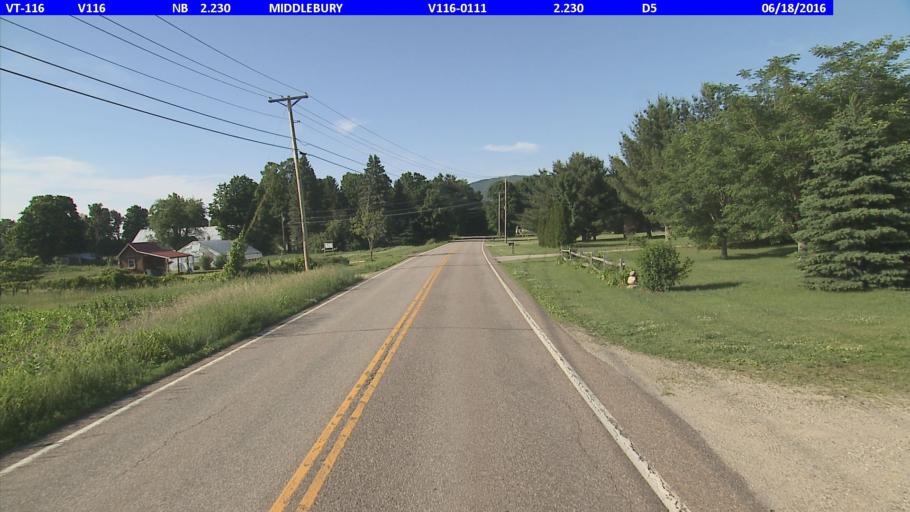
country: US
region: Vermont
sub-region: Addison County
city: Middlebury (village)
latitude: 43.9966
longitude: -73.1042
